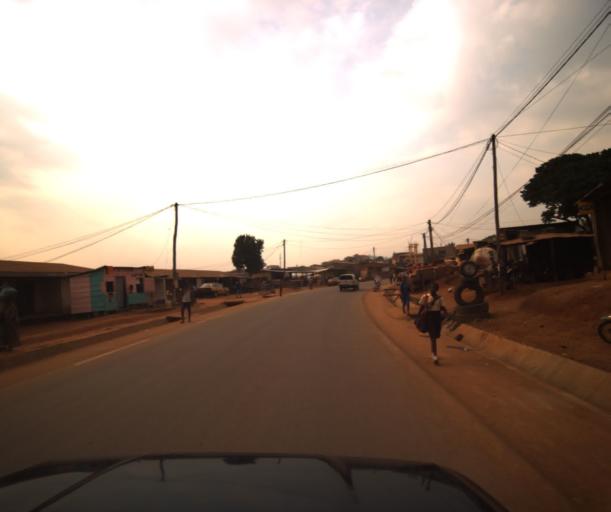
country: CM
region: Centre
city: Yaounde
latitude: 3.8274
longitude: 11.4709
